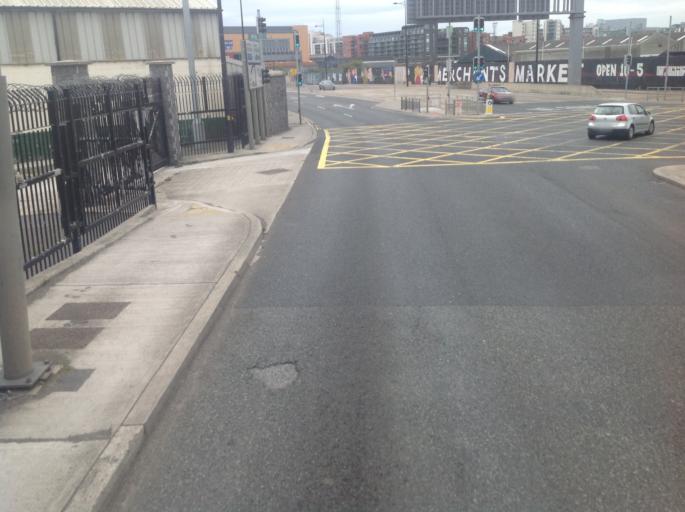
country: IE
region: Leinster
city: Ringsend
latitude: 53.3526
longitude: -6.2244
